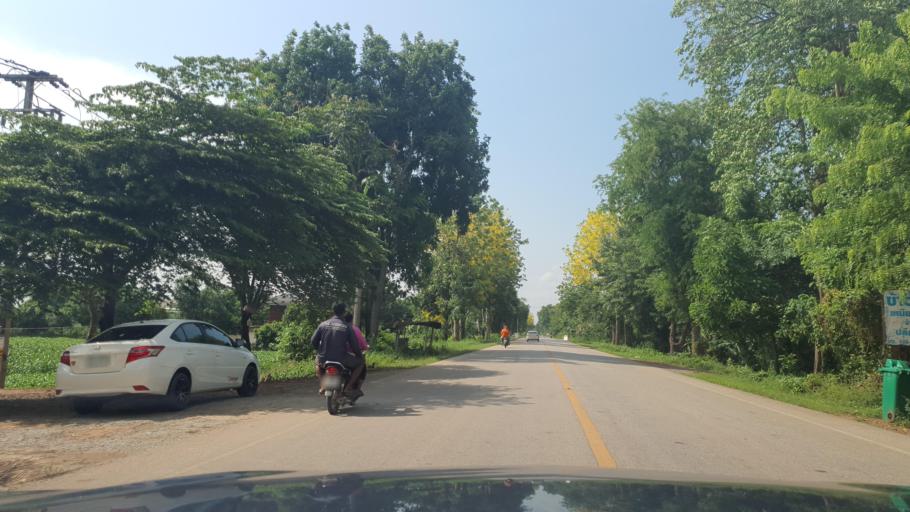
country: TH
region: Sukhothai
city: Si Samrong
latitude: 17.1806
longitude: 99.8518
